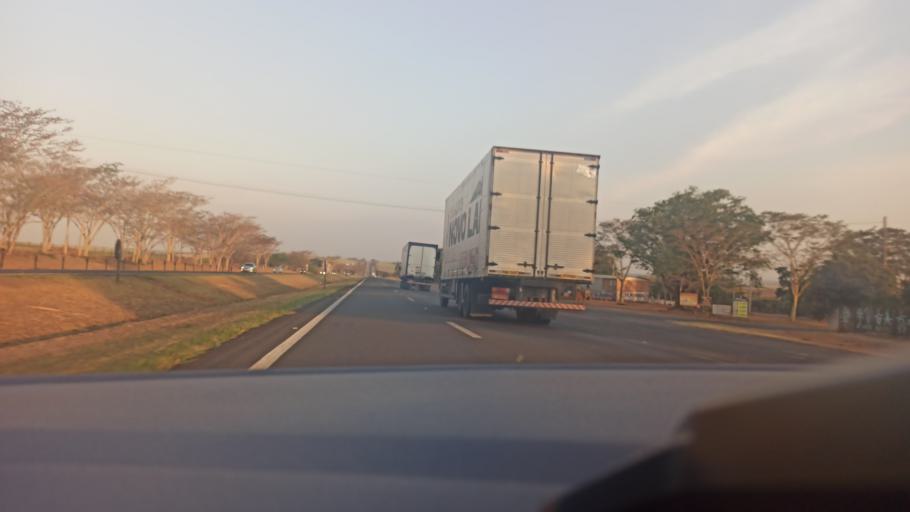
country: BR
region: Sao Paulo
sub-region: Santa Adelia
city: Santa Adelia
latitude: -21.3613
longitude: -48.7635
